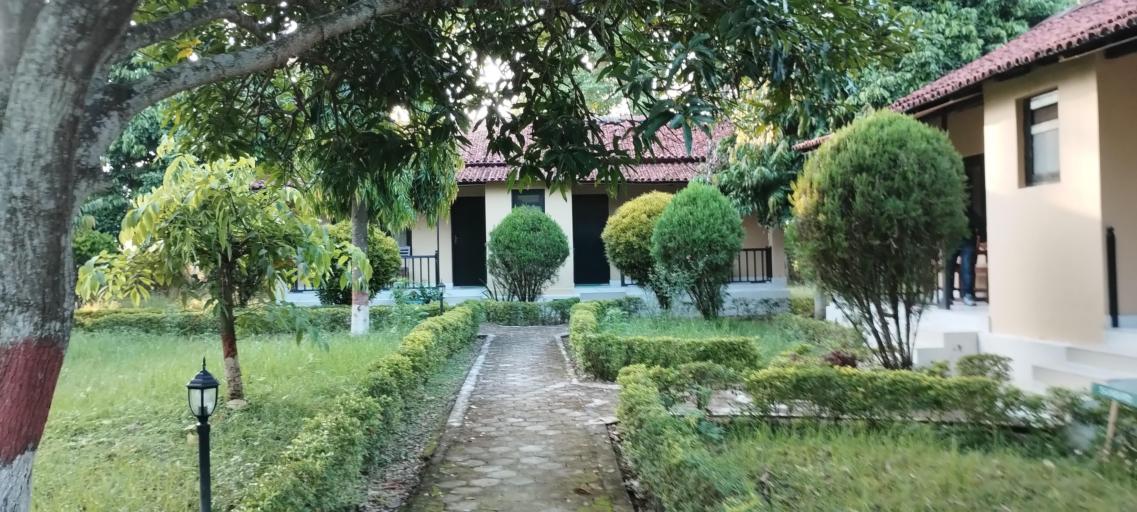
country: NP
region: Far Western
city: Tikapur
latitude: 28.4477
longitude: 81.2400
